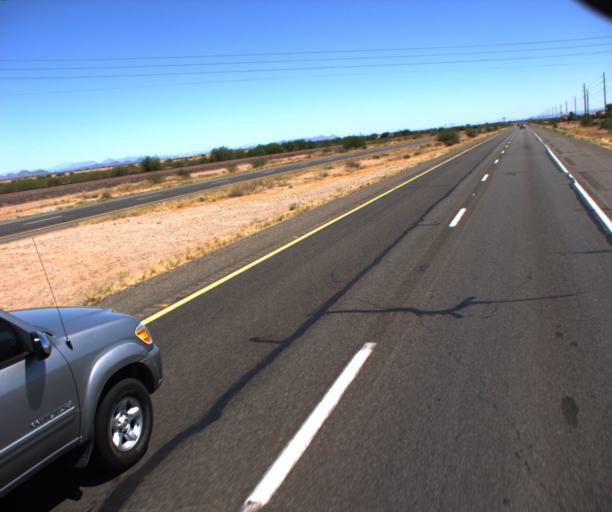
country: US
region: Arizona
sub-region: Maricopa County
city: Sun City West
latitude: 33.7122
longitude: -112.4447
